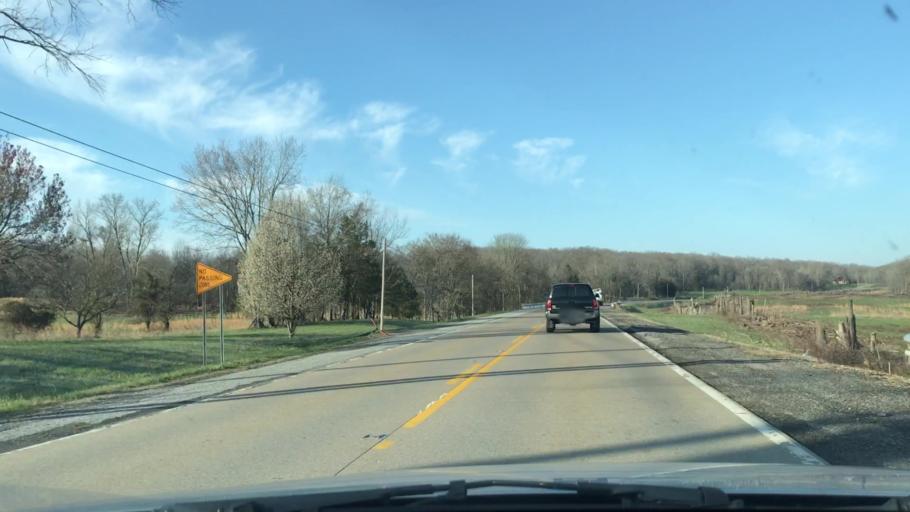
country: US
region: Kentucky
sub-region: Trigg County
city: Cadiz
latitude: 36.8010
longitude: -87.9398
